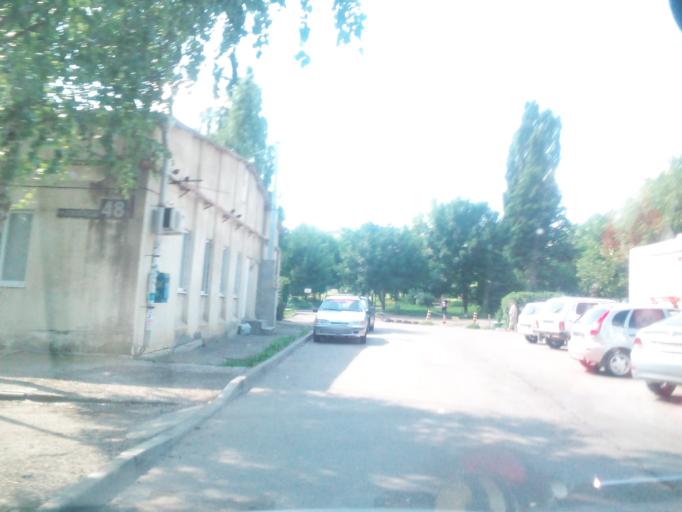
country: RU
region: Stavropol'skiy
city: Pyatigorsk
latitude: 44.0514
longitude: 43.0456
